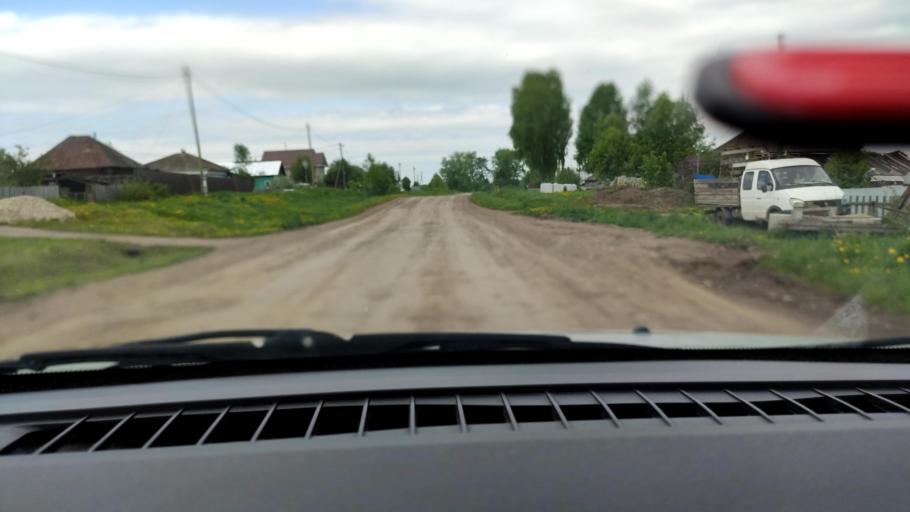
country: RU
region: Perm
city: Bershet'
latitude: 57.7288
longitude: 56.3782
